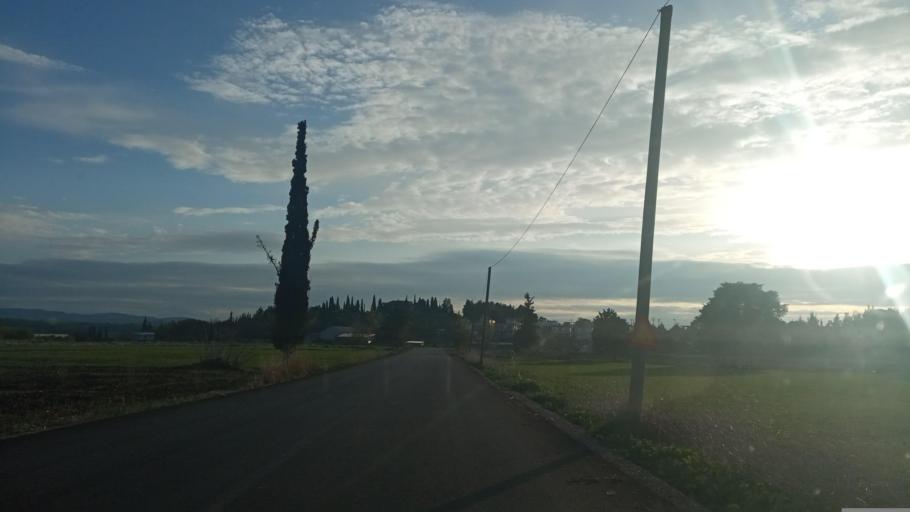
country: GR
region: Central Greece
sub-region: Nomos Evvoias
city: Psachna
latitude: 38.5870
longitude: 23.7163
